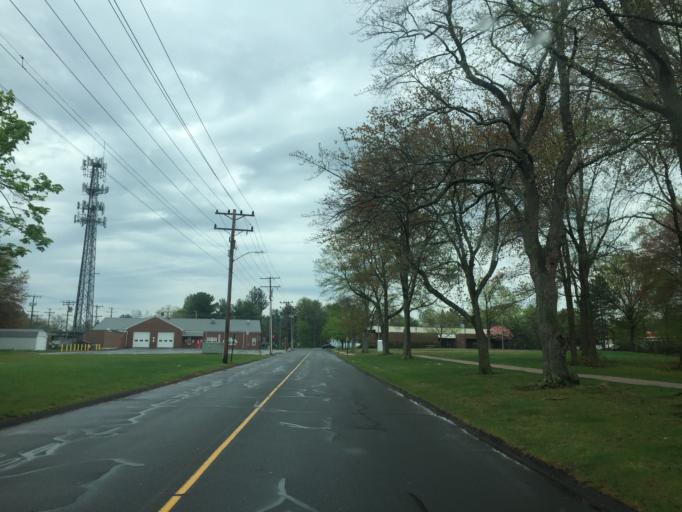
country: US
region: Connecticut
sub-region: Hartford County
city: Blue Hills
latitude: 41.8198
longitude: -72.6982
